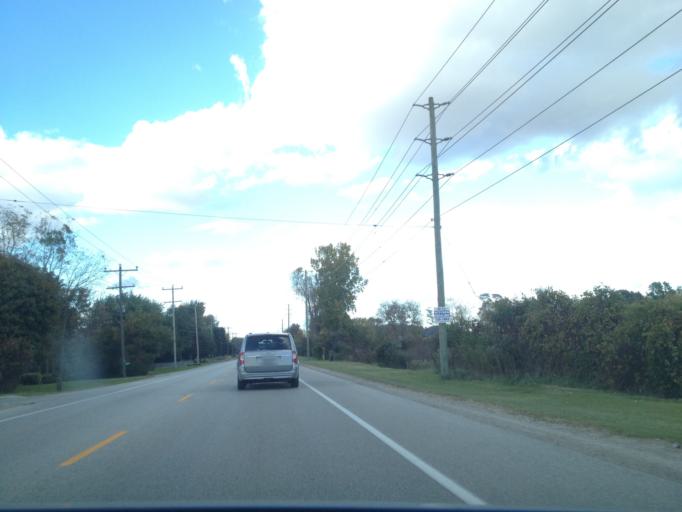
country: CA
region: Ontario
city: Amherstburg
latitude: 42.0598
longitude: -82.7379
